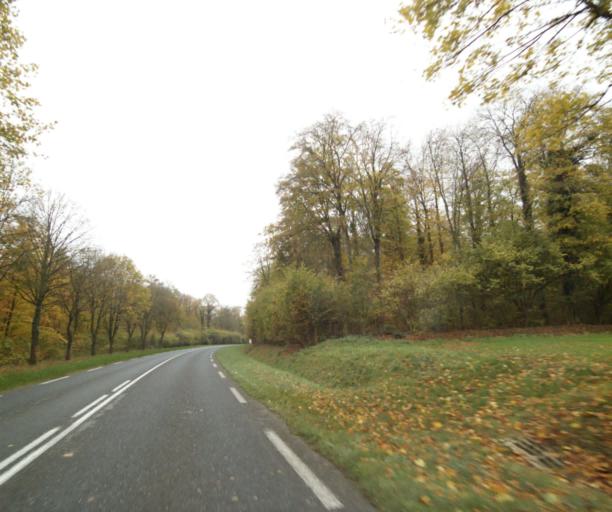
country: FR
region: Lorraine
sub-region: Departement de Meurthe-et-Moselle
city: Briey
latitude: 49.2741
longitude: 5.9587
